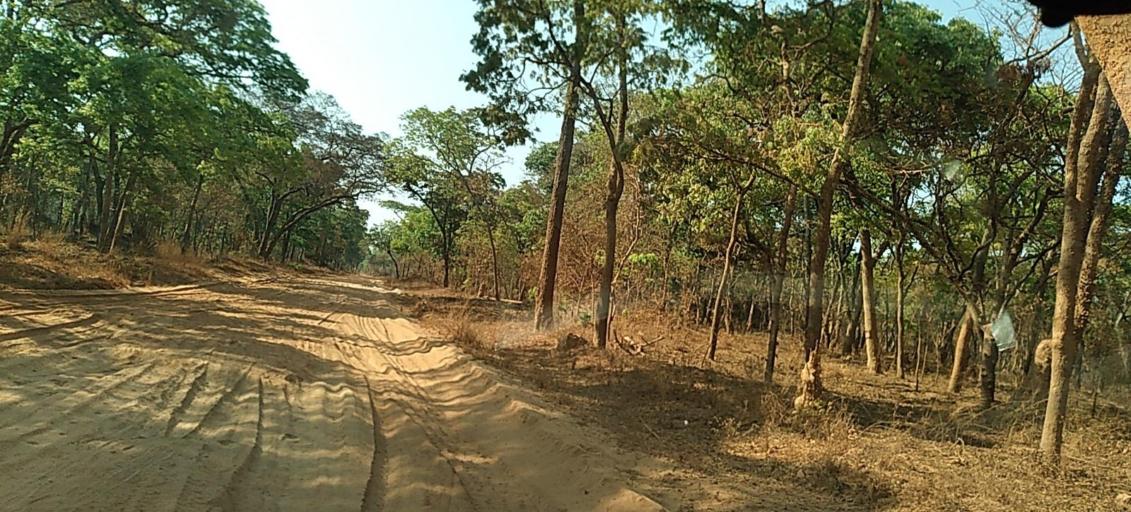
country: ZM
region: North-Western
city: Kasempa
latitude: -13.6785
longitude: 26.0220
